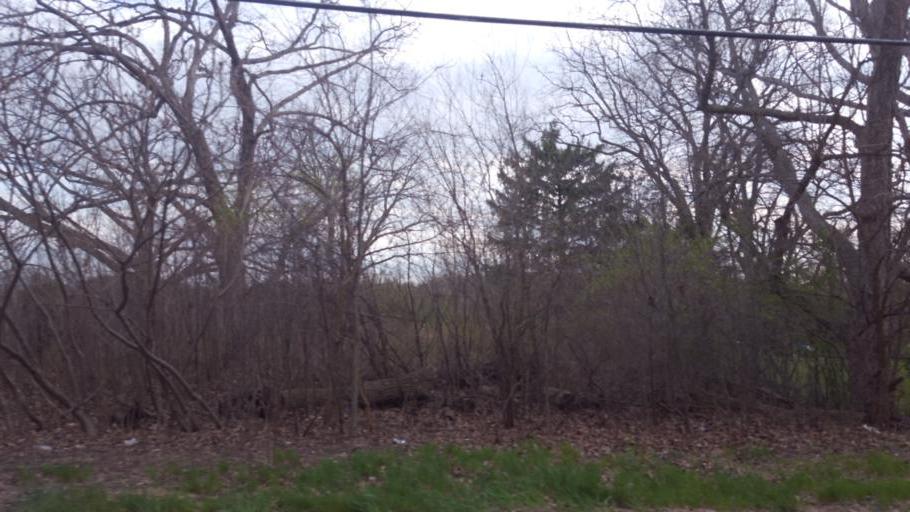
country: US
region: Ohio
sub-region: Erie County
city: Sandusky
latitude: 41.5146
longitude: -82.7556
